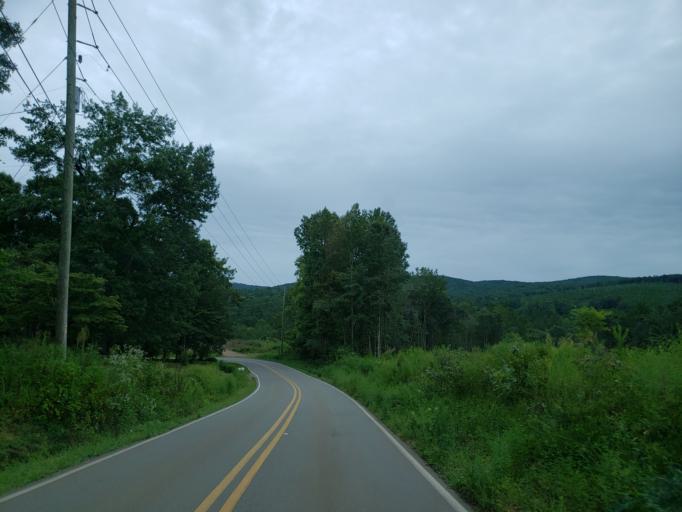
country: US
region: Georgia
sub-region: Pickens County
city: Jasper
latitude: 34.4180
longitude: -84.5568
